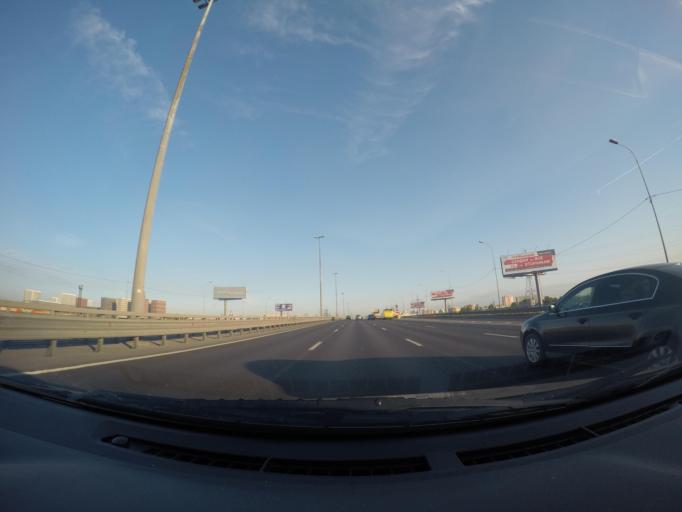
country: RU
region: Moskovskaya
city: Lyubertsy
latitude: 55.6598
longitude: 37.8917
